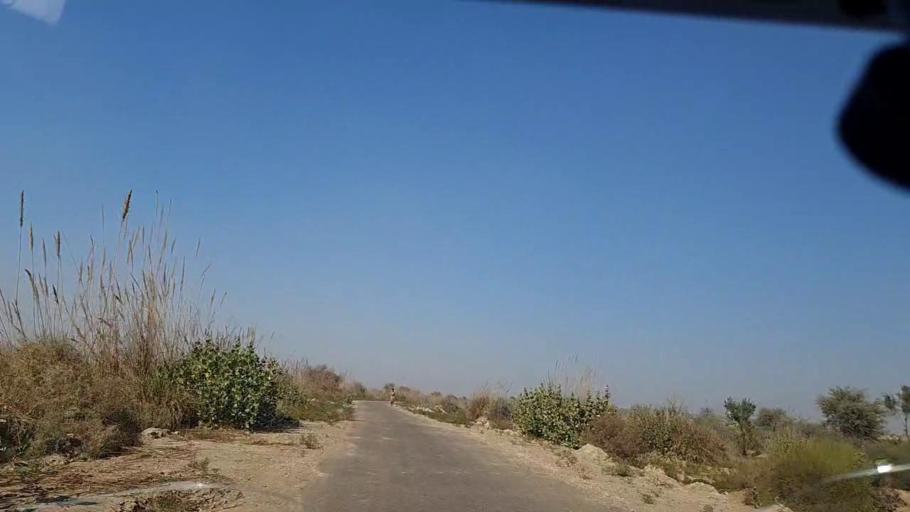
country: PK
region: Sindh
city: Khanpur
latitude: 27.5801
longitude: 69.3771
